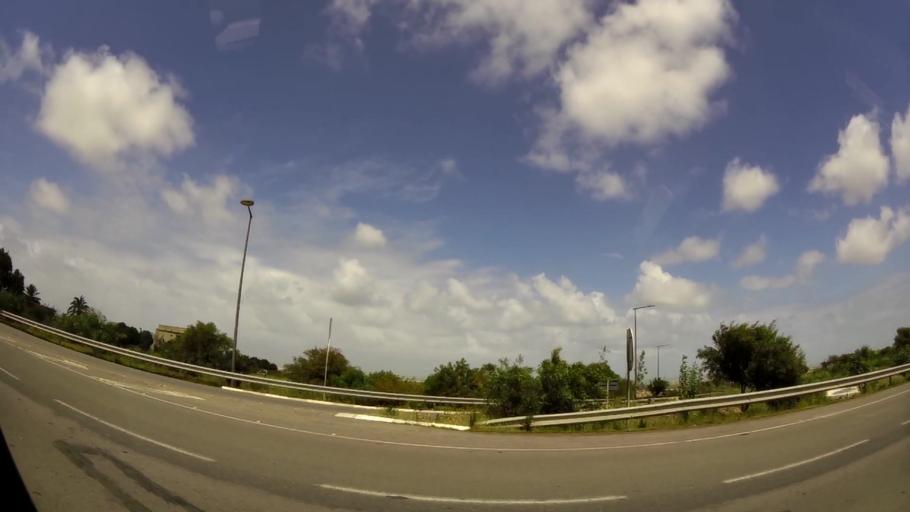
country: MA
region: Grand Casablanca
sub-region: Mediouna
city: Tit Mellil
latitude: 33.6250
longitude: -7.4659
